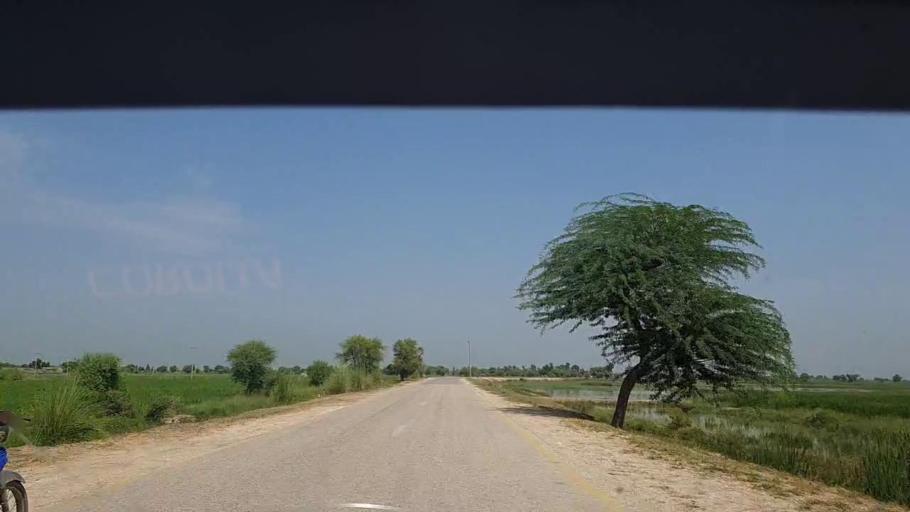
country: PK
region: Sindh
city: Rustam jo Goth
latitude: 28.1046
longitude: 68.8041
